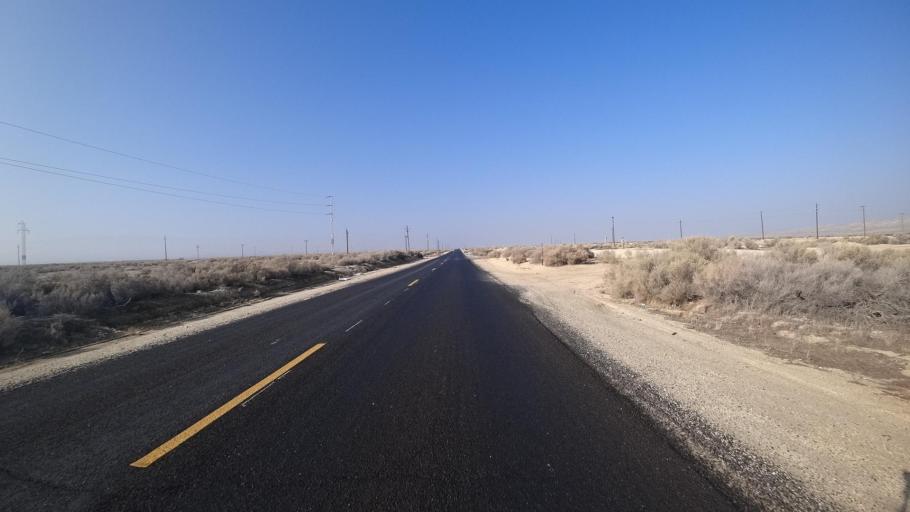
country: US
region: California
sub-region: Kern County
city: Ford City
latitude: 35.1806
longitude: -119.4812
